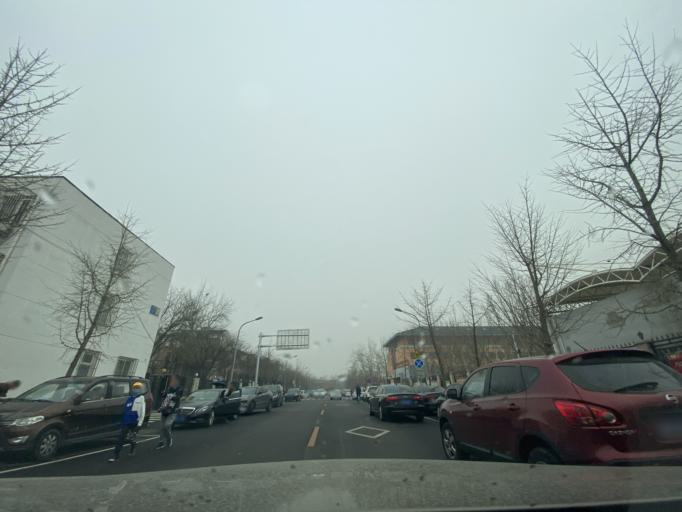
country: CN
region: Beijing
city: Sijiqing
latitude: 39.9545
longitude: 116.2280
